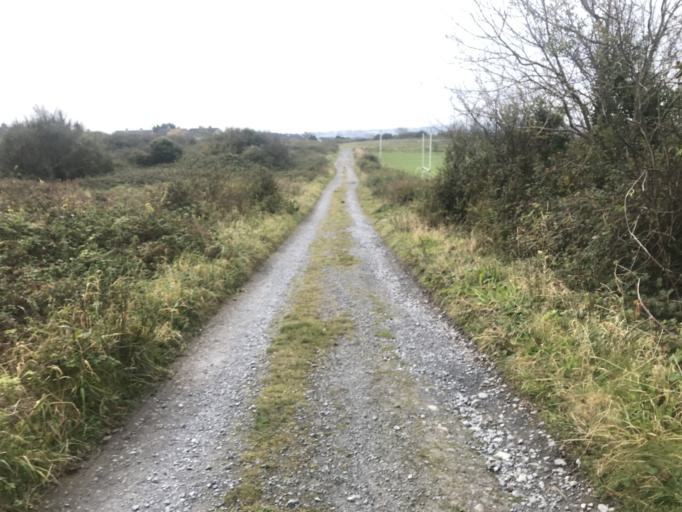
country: IE
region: Connaught
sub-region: County Galway
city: Gaillimh
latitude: 53.2951
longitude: -9.0432
